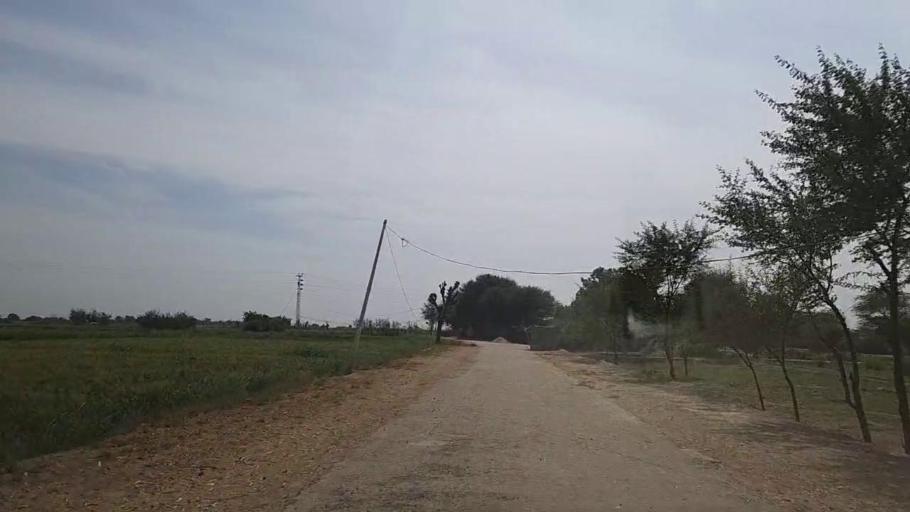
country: PK
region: Sindh
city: Kunri
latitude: 25.2105
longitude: 69.4930
